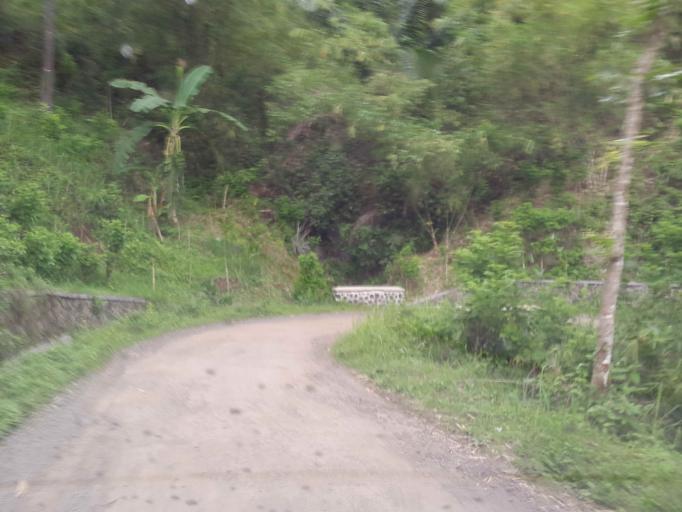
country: ID
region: Central Java
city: Bantarmangu
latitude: -7.3526
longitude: 108.9176
